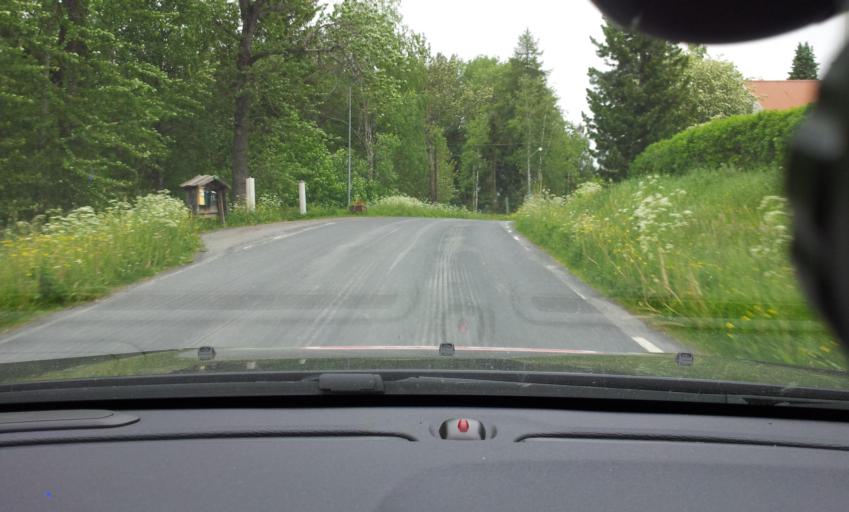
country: SE
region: Jaemtland
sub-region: Are Kommun
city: Jarpen
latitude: 63.2845
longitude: 13.7451
